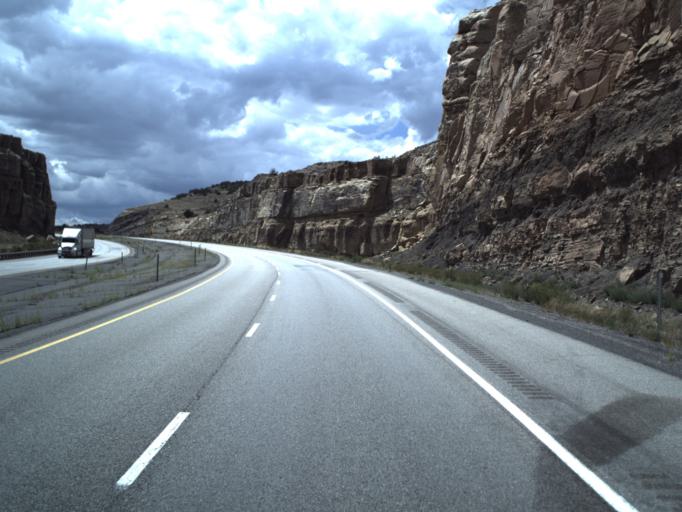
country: US
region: Utah
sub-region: Emery County
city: Ferron
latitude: 38.8054
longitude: -111.2627
